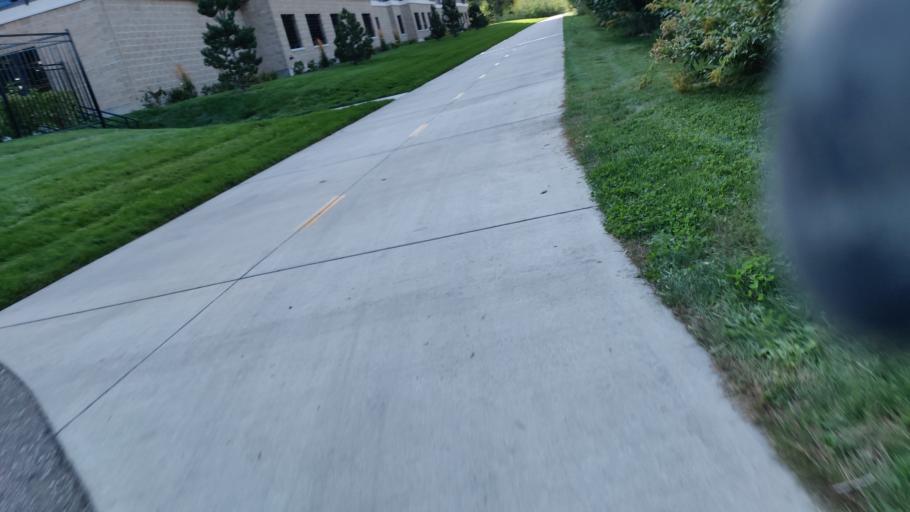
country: US
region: Idaho
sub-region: Ada County
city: Boise
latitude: 43.5779
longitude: -116.1492
